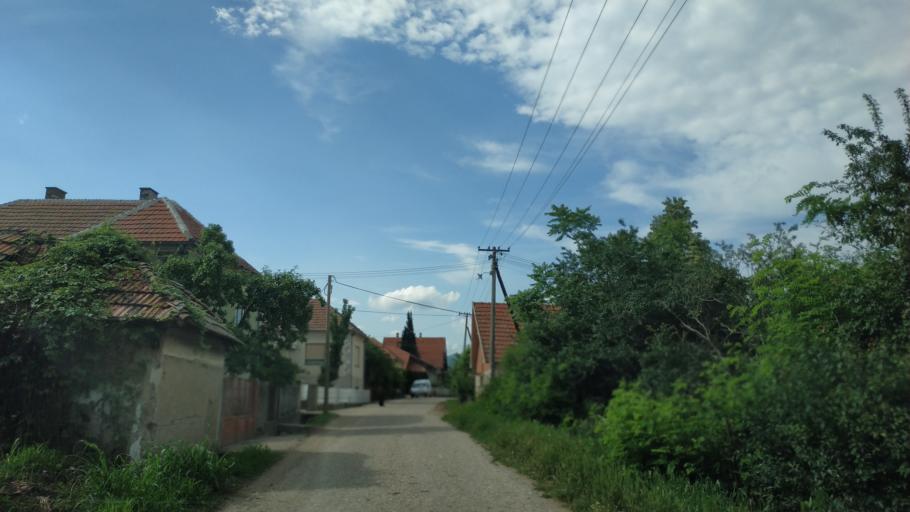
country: RS
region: Central Serbia
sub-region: Nisavski Okrug
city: Aleksinac
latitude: 43.6174
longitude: 21.6463
